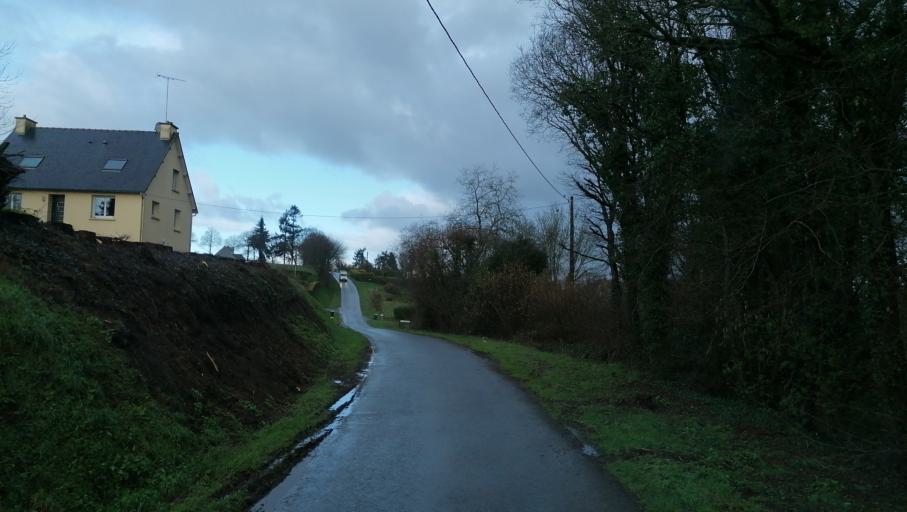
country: FR
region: Brittany
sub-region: Departement des Cotes-d'Armor
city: Plouagat
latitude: 48.4970
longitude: -2.9675
